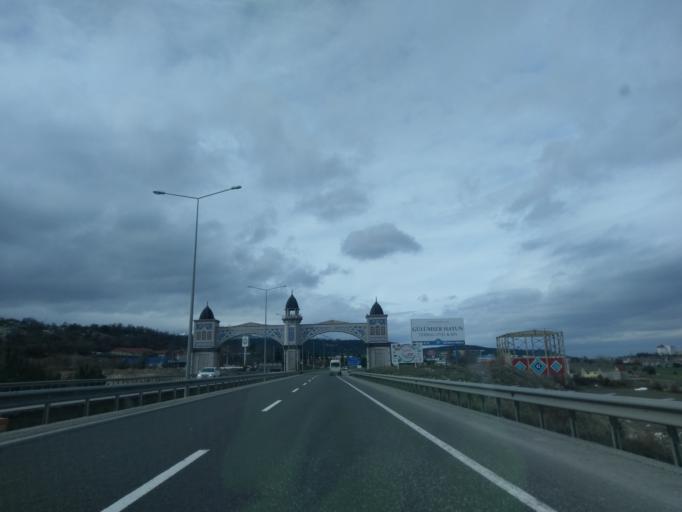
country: TR
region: Kuetahya
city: Kutahya
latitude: 39.3762
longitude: 30.0578
